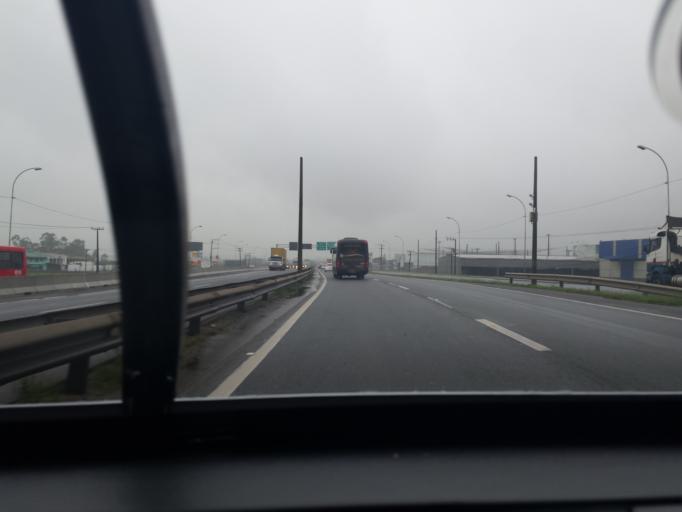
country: BR
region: Santa Catarina
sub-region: Itajai
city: Itajai
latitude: -26.8598
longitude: -48.7279
